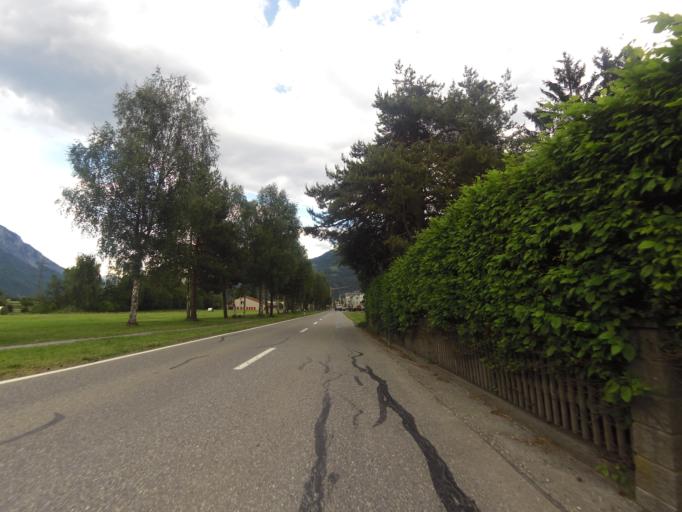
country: CH
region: Grisons
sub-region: Imboden District
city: Bonaduz
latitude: 46.8124
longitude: 9.3892
